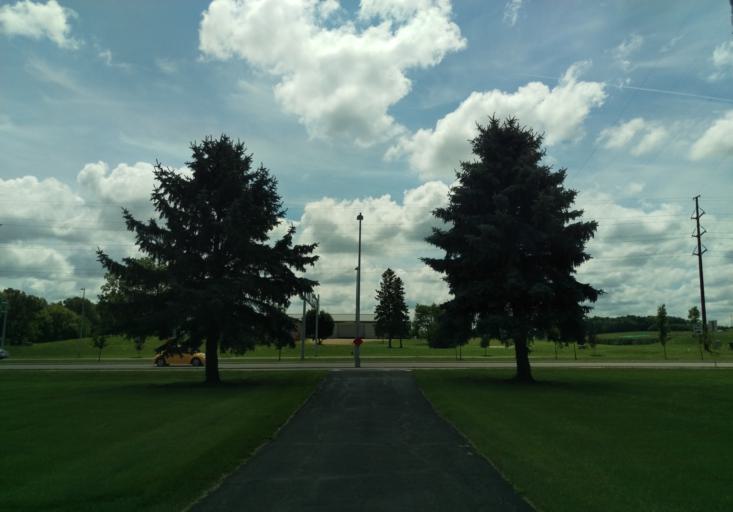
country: US
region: Wisconsin
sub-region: Dane County
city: Middleton
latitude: 43.0608
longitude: -89.5303
